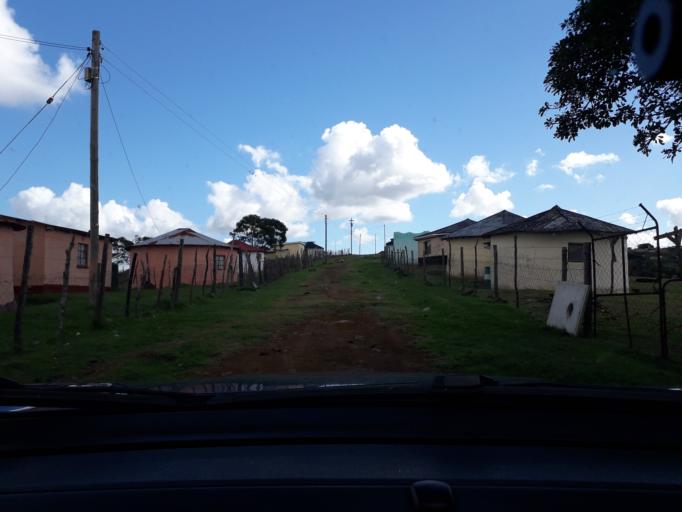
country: ZA
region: Eastern Cape
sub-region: Buffalo City Metropolitan Municipality
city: Bhisho
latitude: -33.1177
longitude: 27.4349
